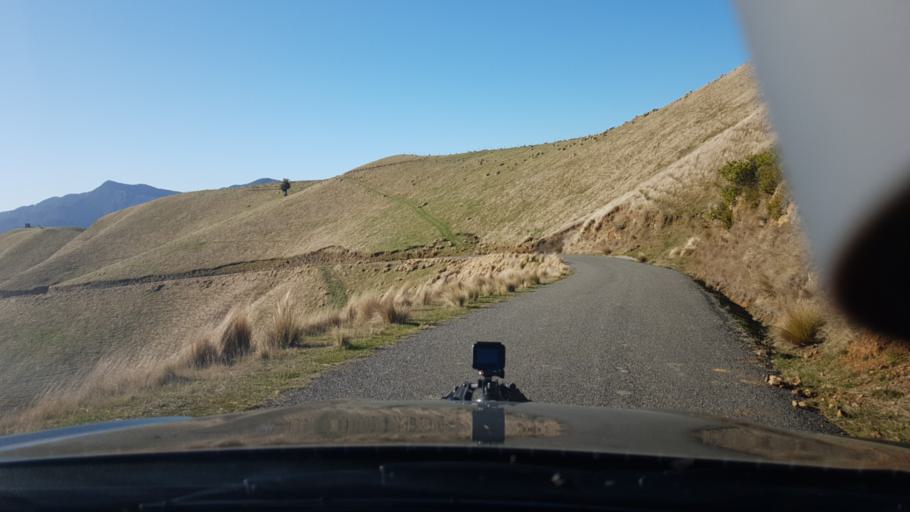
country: NZ
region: Marlborough
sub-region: Marlborough District
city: Picton
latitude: -40.9521
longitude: 173.8296
